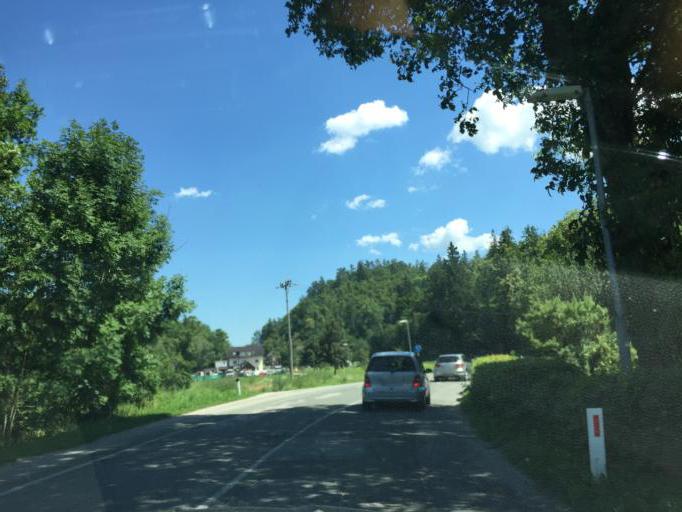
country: SI
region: Bled
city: Bled
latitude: 46.3740
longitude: 14.0973
